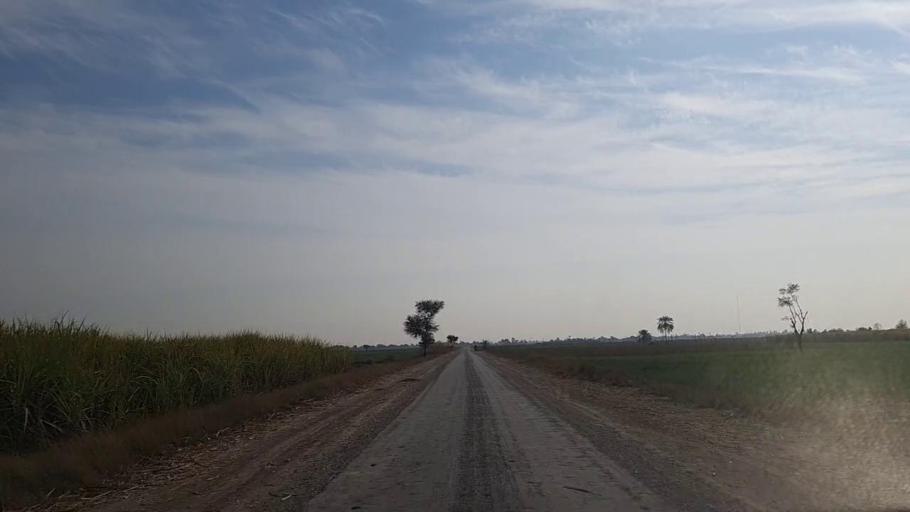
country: PK
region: Sindh
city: Daur
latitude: 26.4841
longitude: 68.4129
